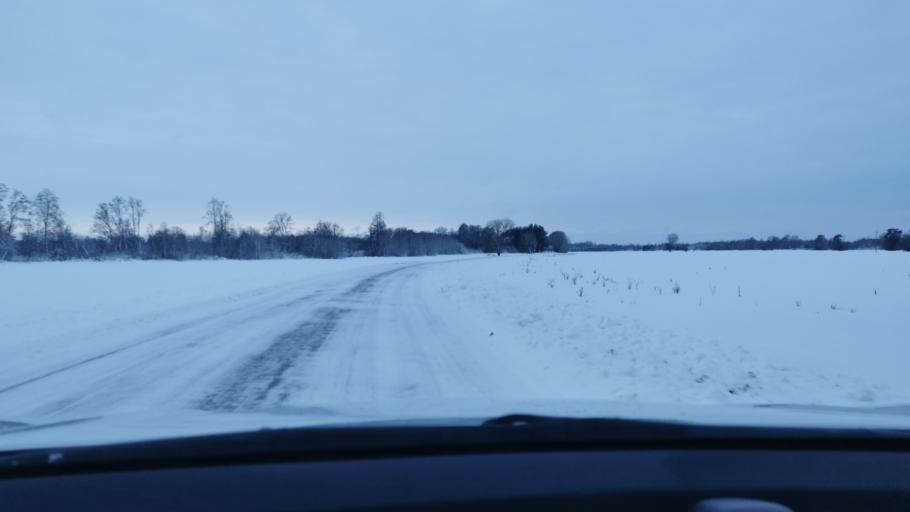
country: EE
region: Laeaene-Virumaa
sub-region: Viru-Nigula vald
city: Kunda
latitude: 59.4536
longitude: 26.5254
